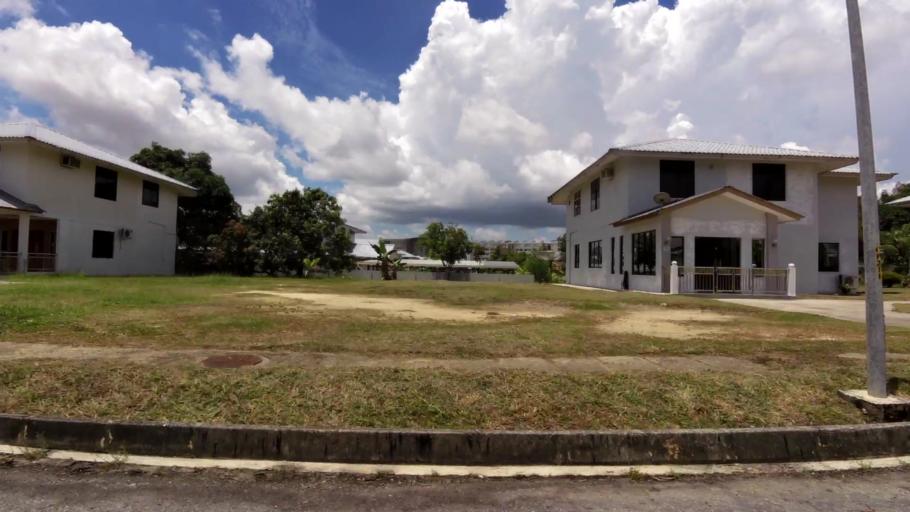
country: BN
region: Brunei and Muara
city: Bandar Seri Begawan
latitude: 4.9607
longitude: 114.9123
